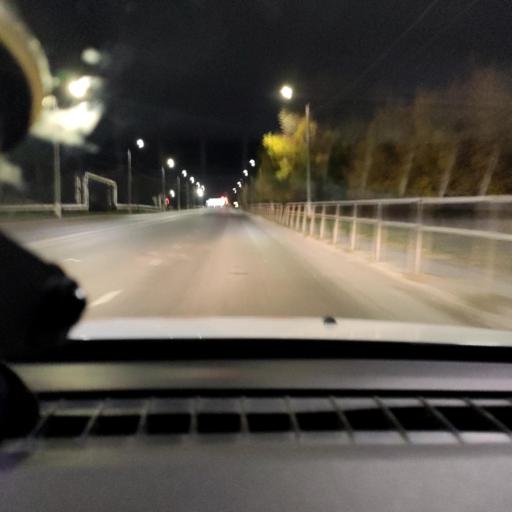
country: RU
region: Samara
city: Novokuybyshevsk
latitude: 53.0933
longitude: 49.9406
